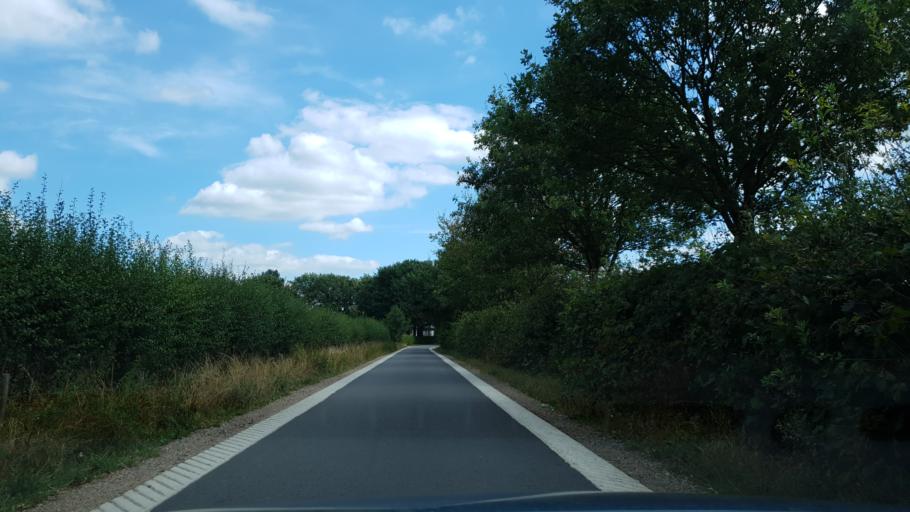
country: NL
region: Gelderland
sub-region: Gemeente Nijmegen
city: Lindenholt
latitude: 51.7818
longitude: 5.8162
